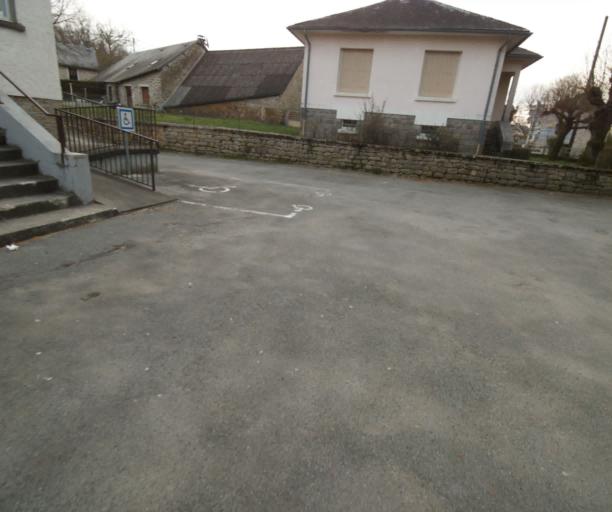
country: FR
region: Limousin
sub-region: Departement de la Correze
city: Correze
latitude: 45.4243
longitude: 1.8372
